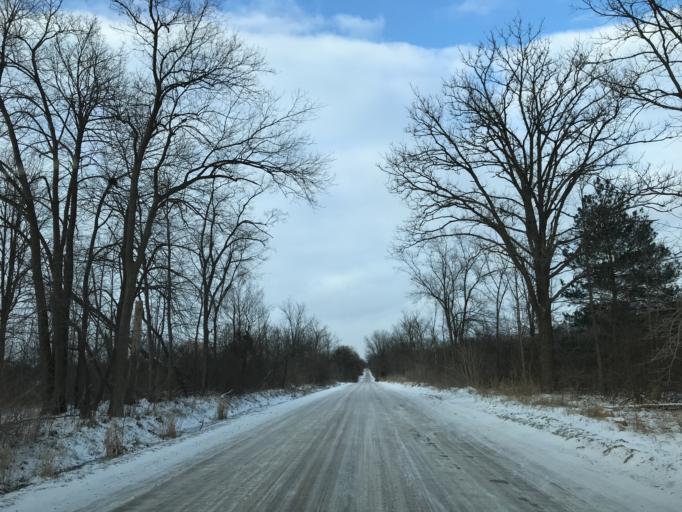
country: US
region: Michigan
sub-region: Oakland County
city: South Lyon
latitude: 42.4504
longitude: -83.5920
